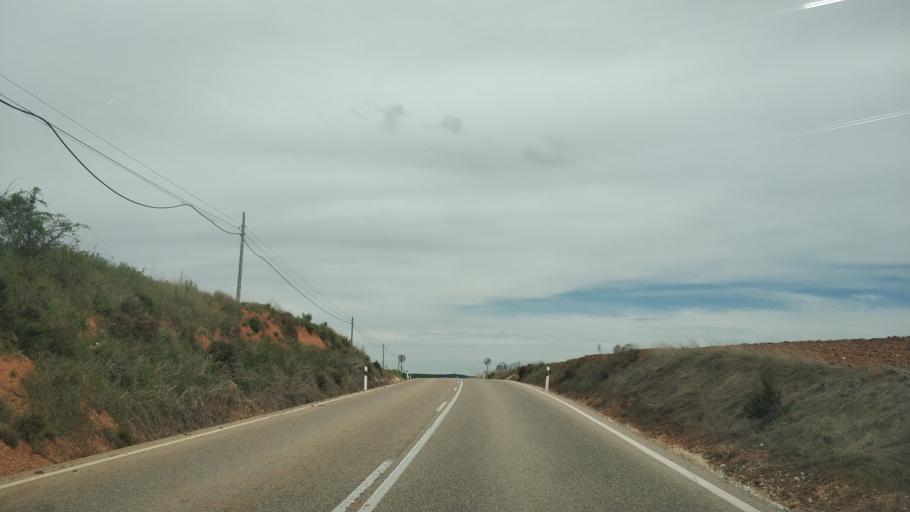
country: ES
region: Castille and Leon
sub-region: Provincia de Soria
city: El Burgo de Osma
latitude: 41.5760
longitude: -3.0265
